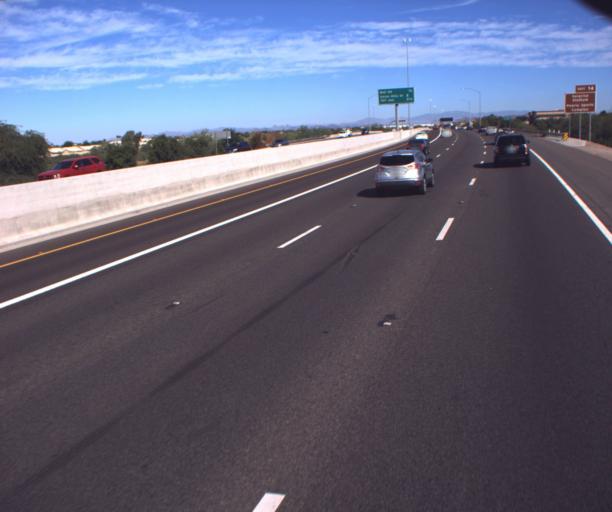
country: US
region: Arizona
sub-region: Maricopa County
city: Peoria
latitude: 33.6188
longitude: -112.2391
